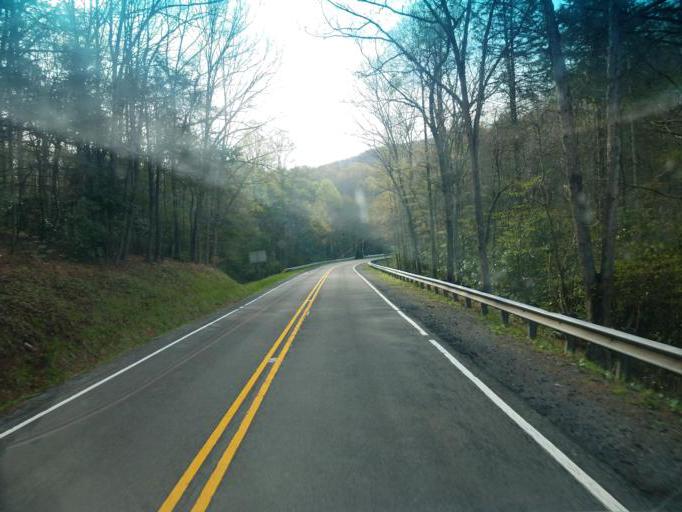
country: US
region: Virginia
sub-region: Smyth County
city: Atkins
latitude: 36.8102
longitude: -81.4059
